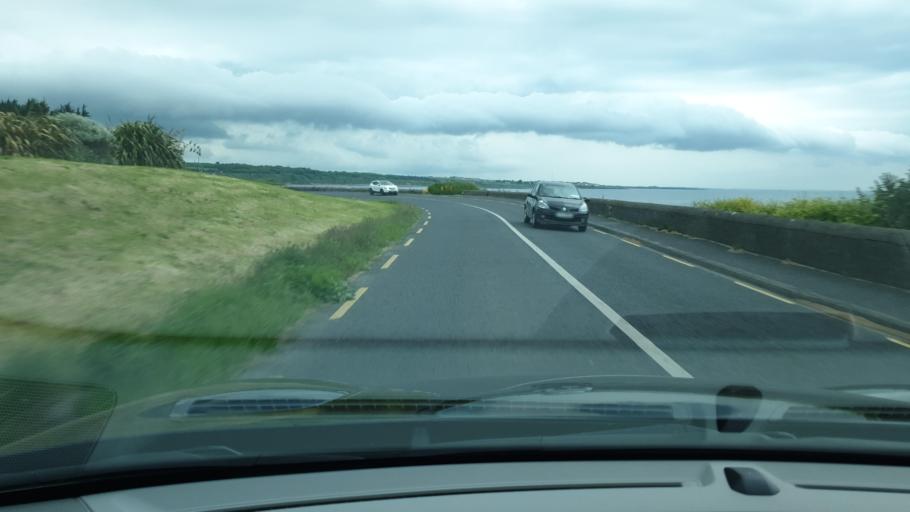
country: IE
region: Leinster
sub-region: Fingal County
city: Skerries
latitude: 53.5854
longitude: -6.1292
